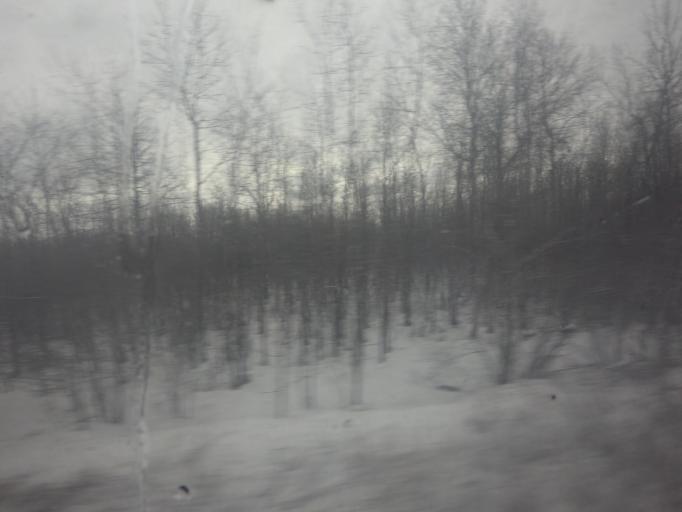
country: CA
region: Ontario
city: Bells Corners
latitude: 45.1659
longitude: -75.8352
